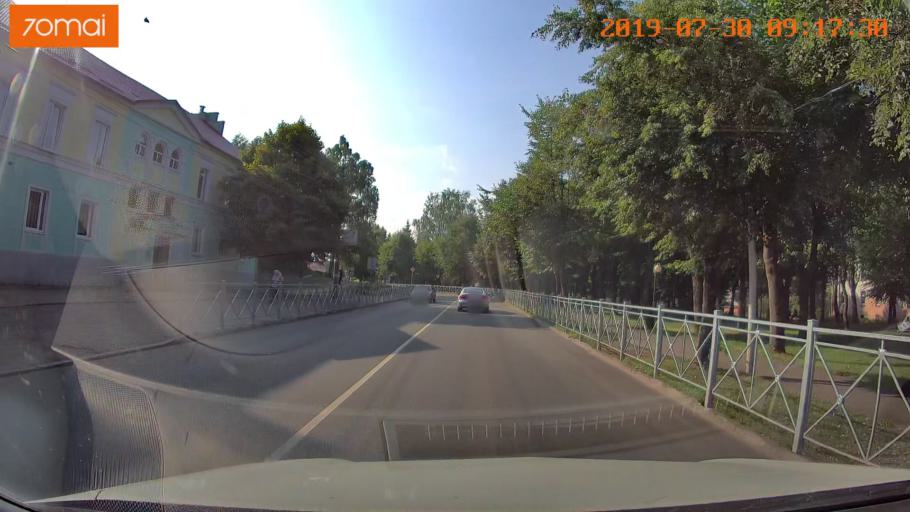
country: RU
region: Kaliningrad
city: Nesterov
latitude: 54.6335
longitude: 22.5687
